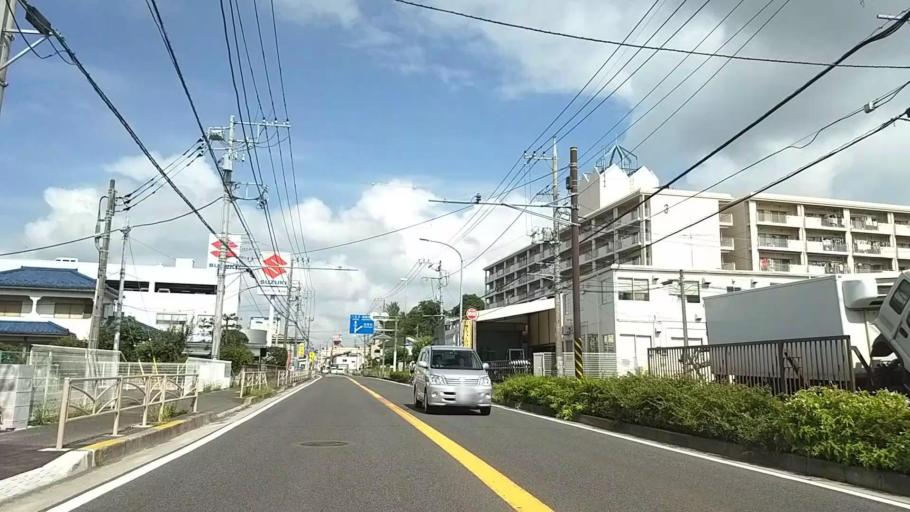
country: JP
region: Kanagawa
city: Minami-rinkan
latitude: 35.4930
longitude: 139.5107
